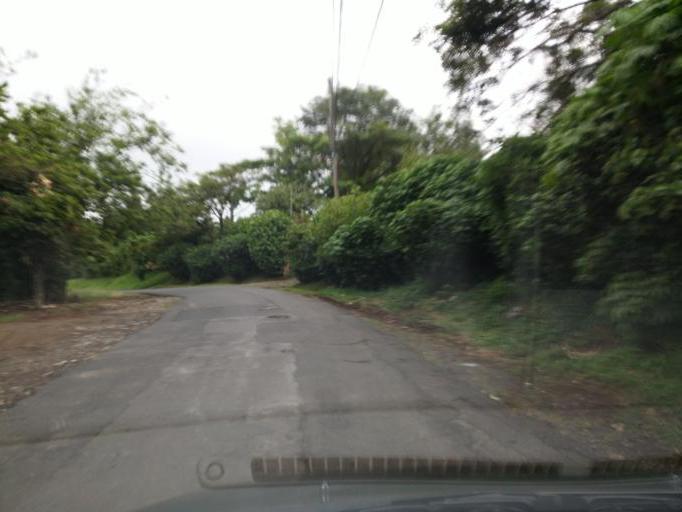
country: CR
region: Heredia
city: San Josecito
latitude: 10.0430
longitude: -84.1061
